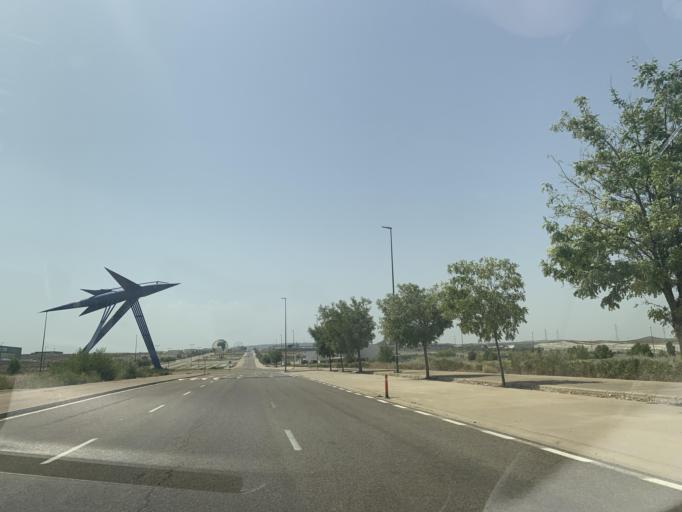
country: ES
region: Aragon
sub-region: Provincia de Zaragoza
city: Zaragoza
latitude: 41.5838
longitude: -0.8409
